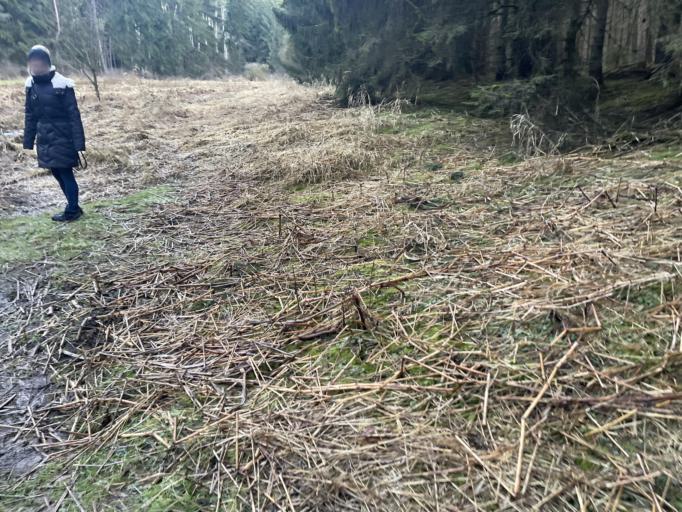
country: DE
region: Bavaria
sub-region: Lower Bavaria
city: Biburg
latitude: 48.8269
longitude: 11.9115
